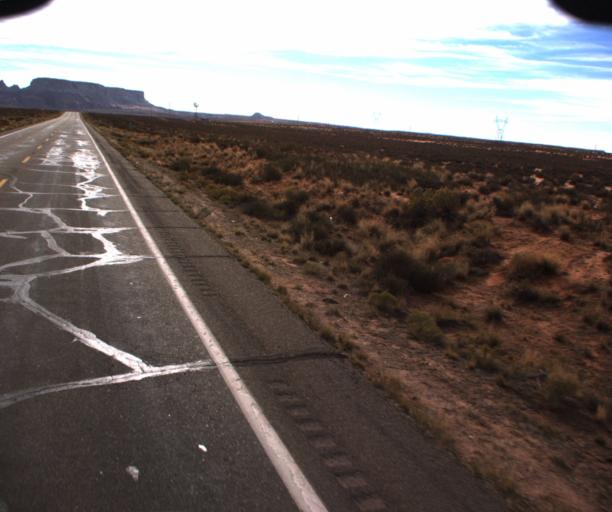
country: US
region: Arizona
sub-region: Coconino County
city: LeChee
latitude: 36.8881
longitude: -111.3645
